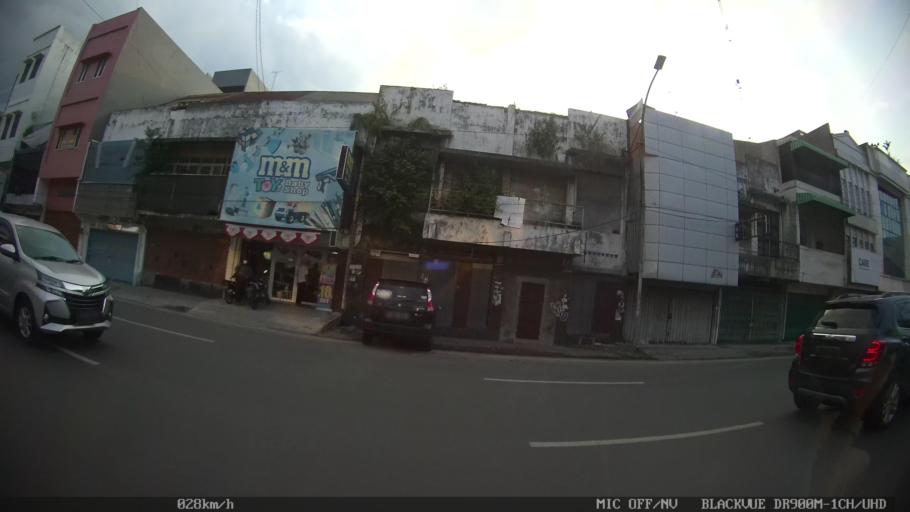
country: ID
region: North Sumatra
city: Medan
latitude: 3.5926
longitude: 98.6837
